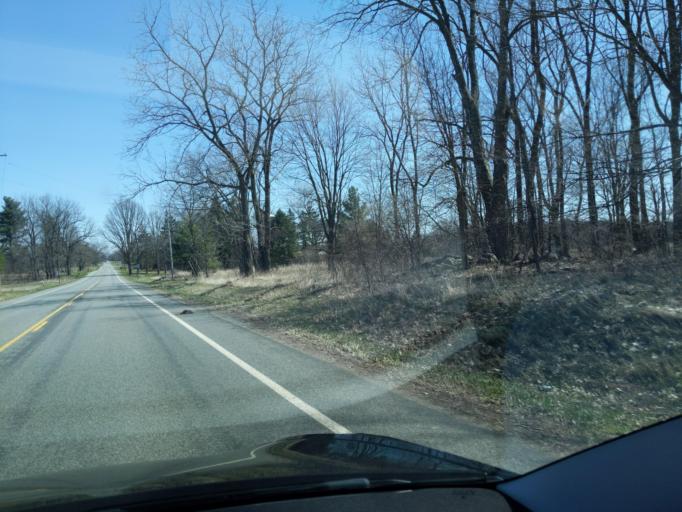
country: US
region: Michigan
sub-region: Ingham County
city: Holt
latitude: 42.5821
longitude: -84.5596
